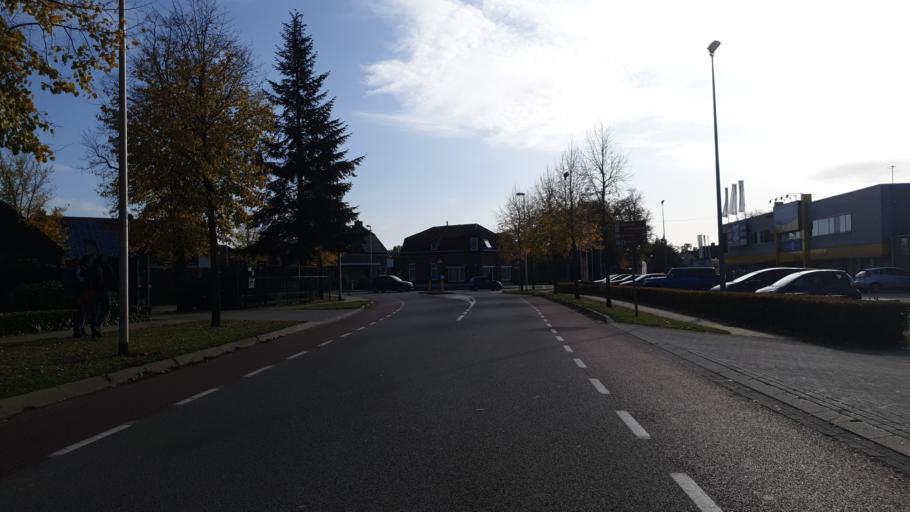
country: NL
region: Limburg
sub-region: Gemeente Gennep
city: Gennep
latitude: 51.7068
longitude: 5.9724
